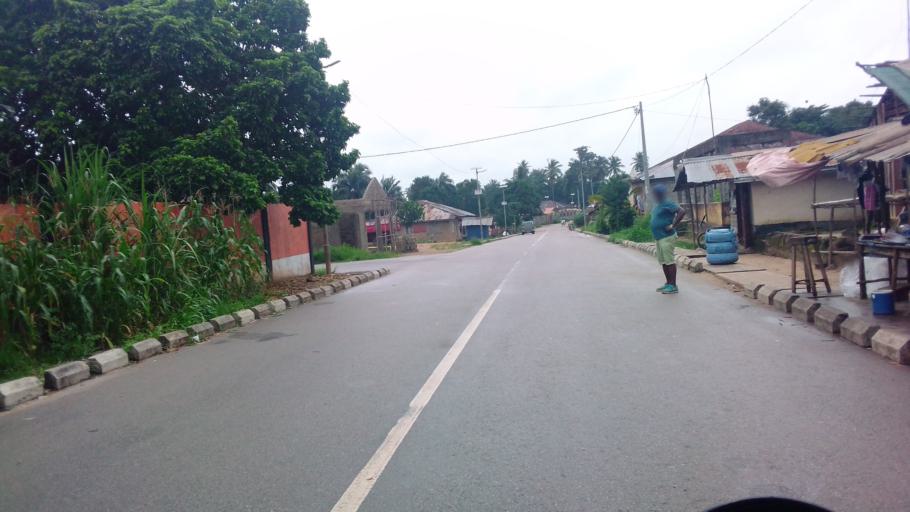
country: SL
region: Northern Province
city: Lunsar
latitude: 8.6841
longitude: -12.5347
